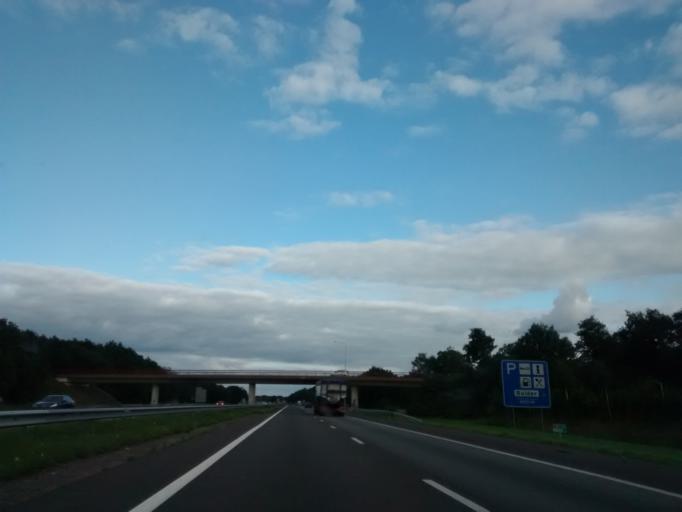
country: NL
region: Gelderland
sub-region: Gemeente Lochem
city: Laren
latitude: 52.2511
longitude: 6.4151
